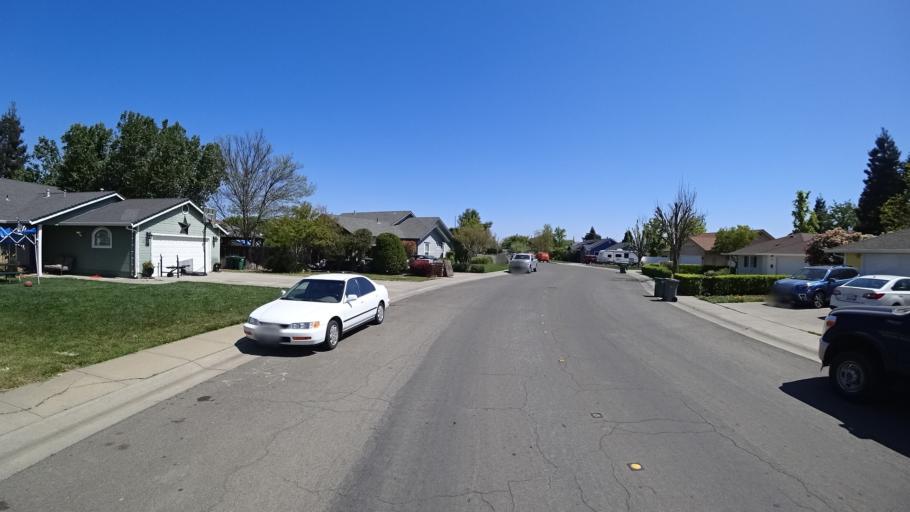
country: US
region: California
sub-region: Glenn County
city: Willows
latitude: 39.5291
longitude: -122.2063
